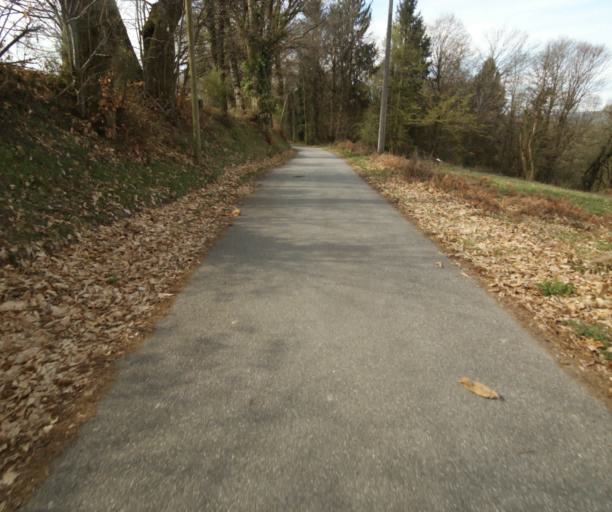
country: FR
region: Limousin
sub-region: Departement de la Correze
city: Correze
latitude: 45.3506
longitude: 1.8589
